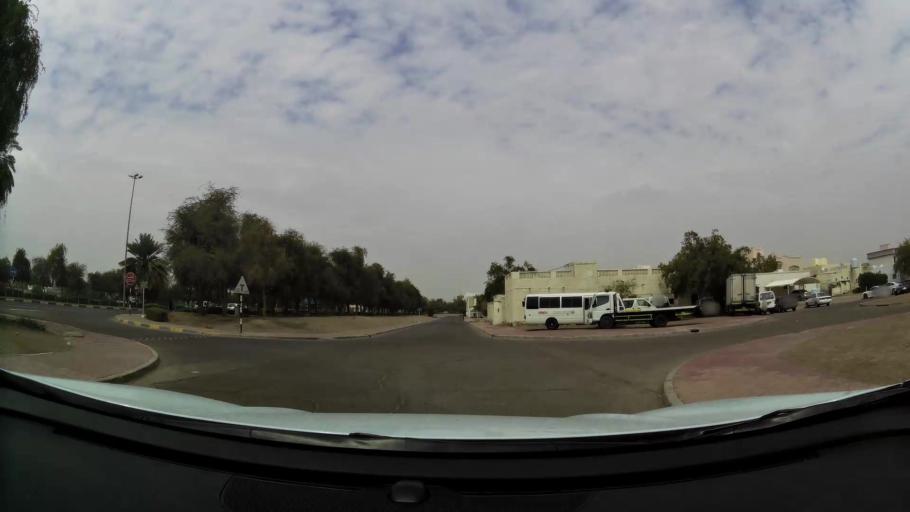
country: AE
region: Abu Dhabi
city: Al Ain
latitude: 24.2125
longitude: 55.7872
